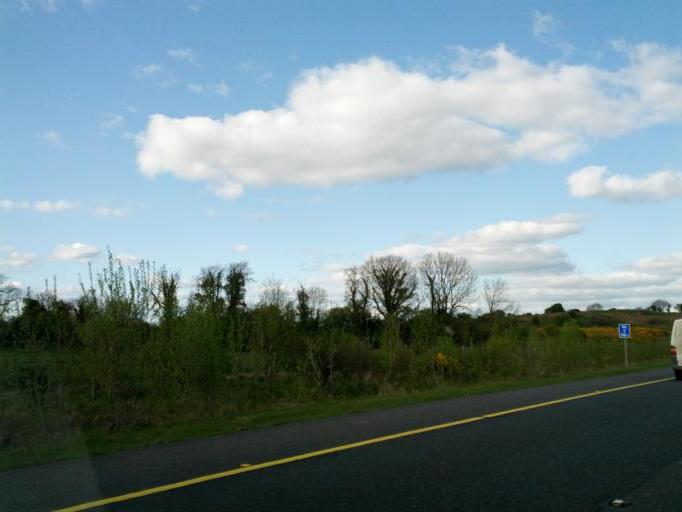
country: IE
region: Leinster
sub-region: An Iarmhi
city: Athlone
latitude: 53.4100
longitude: -8.0169
